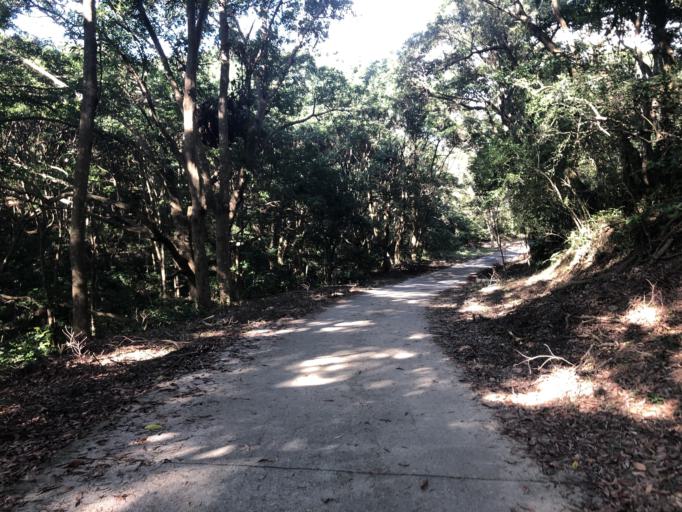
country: HK
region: Tsuen Wan
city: Tsuen Wan
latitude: 22.3893
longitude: 114.0842
